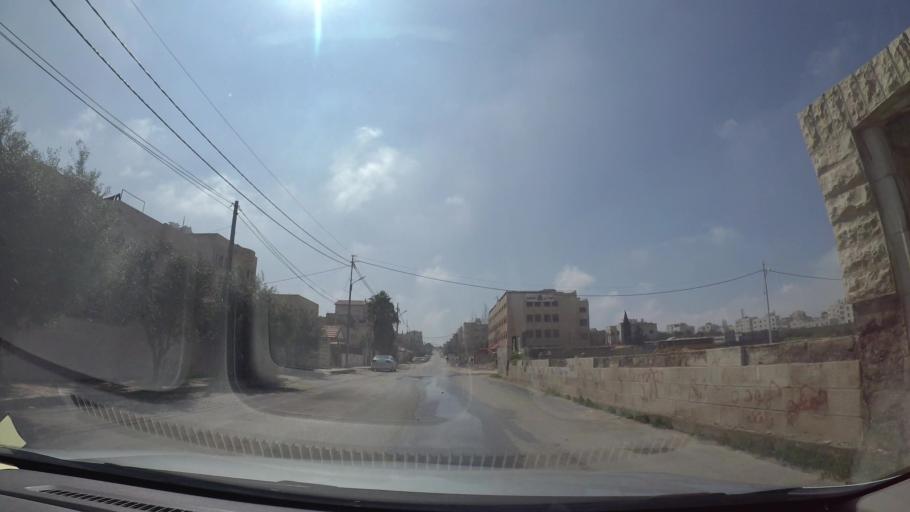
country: JO
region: Amman
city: Al Bunayyat ash Shamaliyah
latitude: 31.8985
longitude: 35.8934
